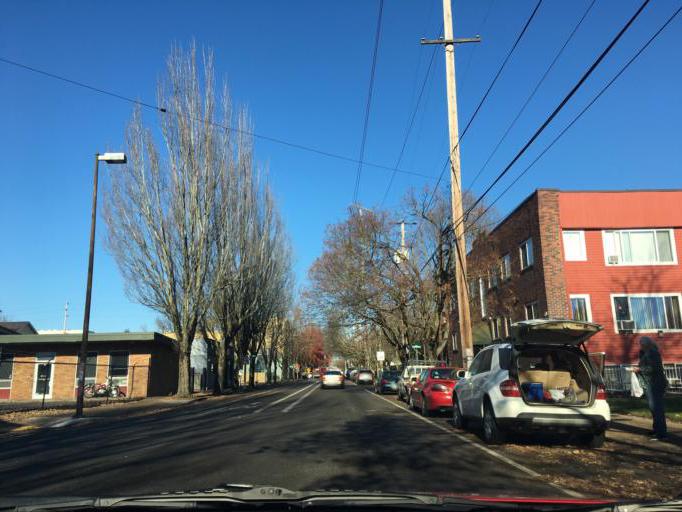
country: US
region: Oregon
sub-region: Multnomah County
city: Portland
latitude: 45.5394
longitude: -122.6667
